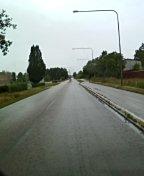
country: SE
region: Vaestmanland
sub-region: Kopings Kommun
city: Koping
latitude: 59.5007
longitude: 16.0107
